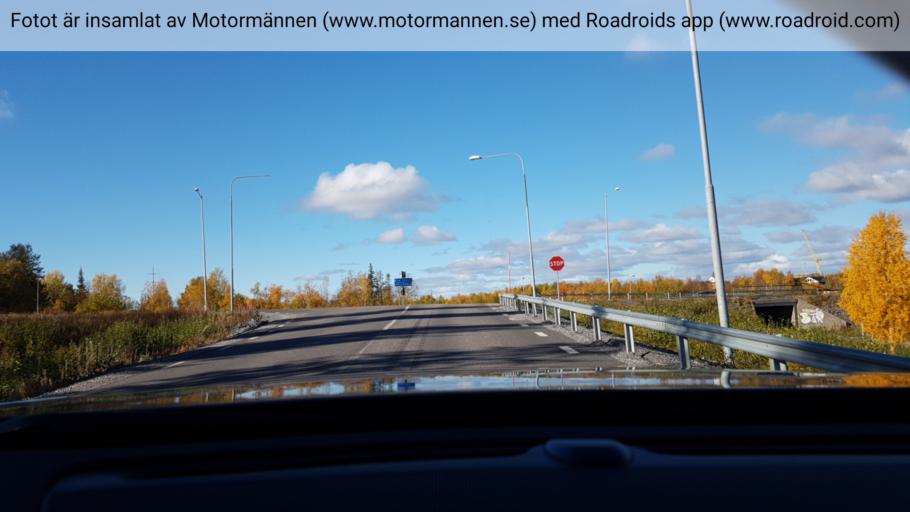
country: SE
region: Norrbotten
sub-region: Gallivare Kommun
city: Gaellivare
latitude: 67.1269
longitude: 20.6707
